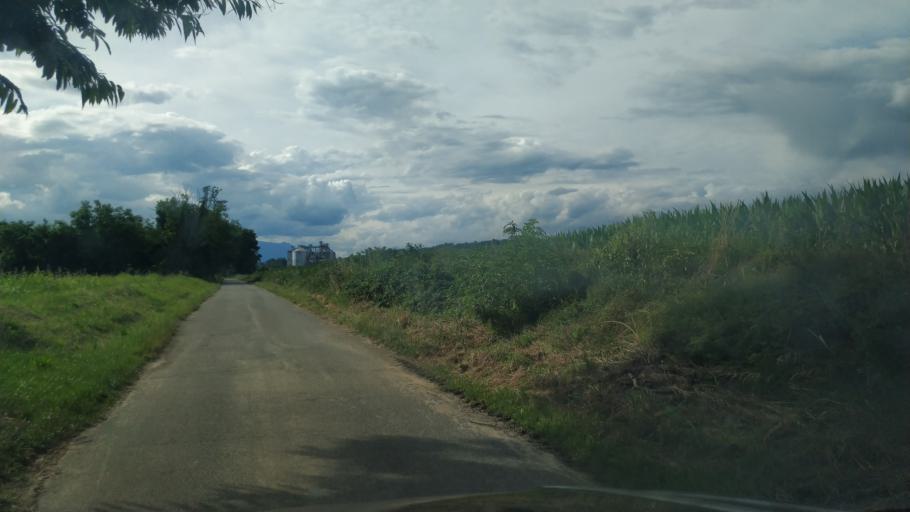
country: IT
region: Piedmont
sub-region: Provincia di Torino
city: Villareggia
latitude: 45.2999
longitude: 7.9826
